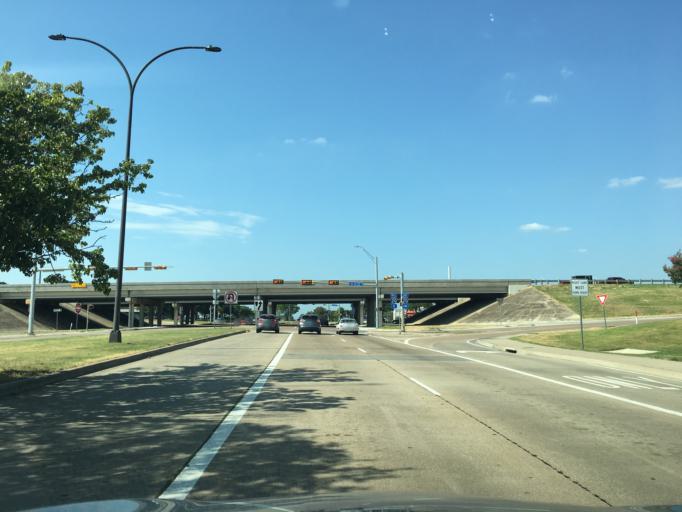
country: US
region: Texas
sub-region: Tarrant County
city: Dalworthington Gardens
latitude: 32.6734
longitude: -97.1496
